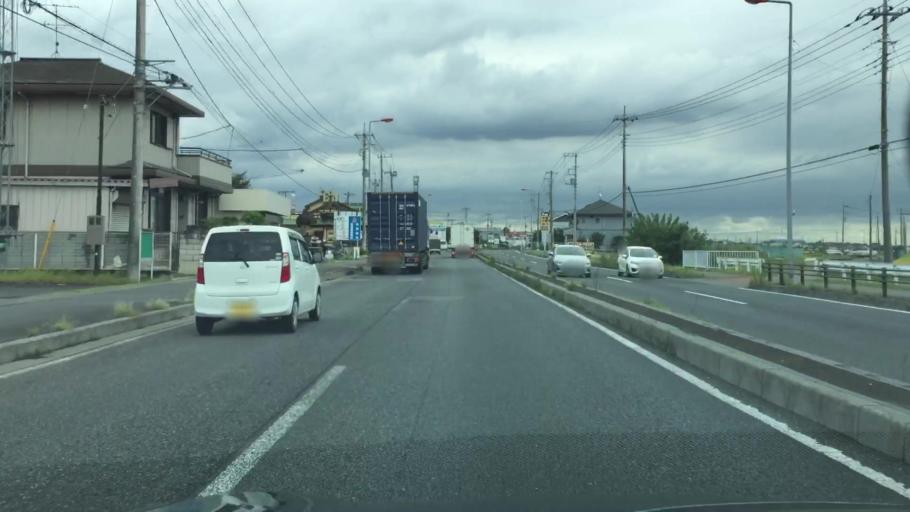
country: JP
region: Saitama
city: Kawagoe
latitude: 35.9158
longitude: 139.5233
